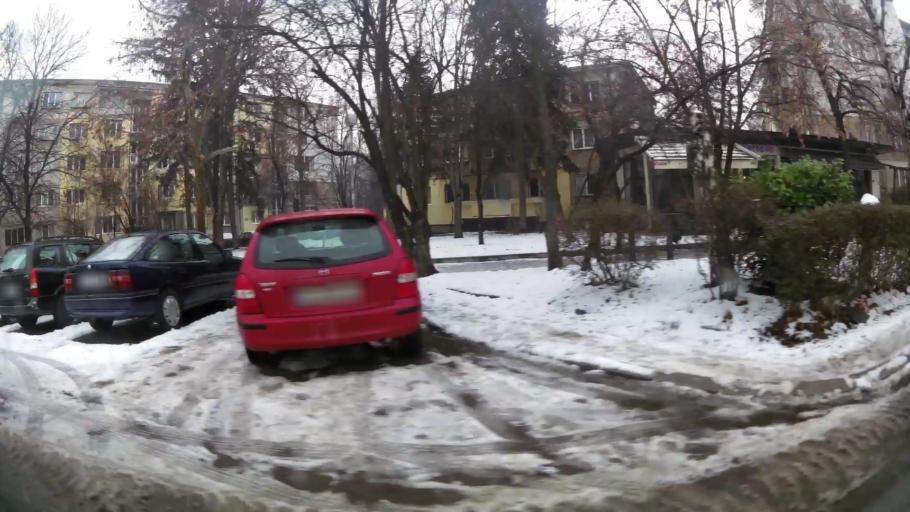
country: BG
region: Sofia-Capital
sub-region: Stolichna Obshtina
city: Sofia
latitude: 42.6820
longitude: 23.2936
